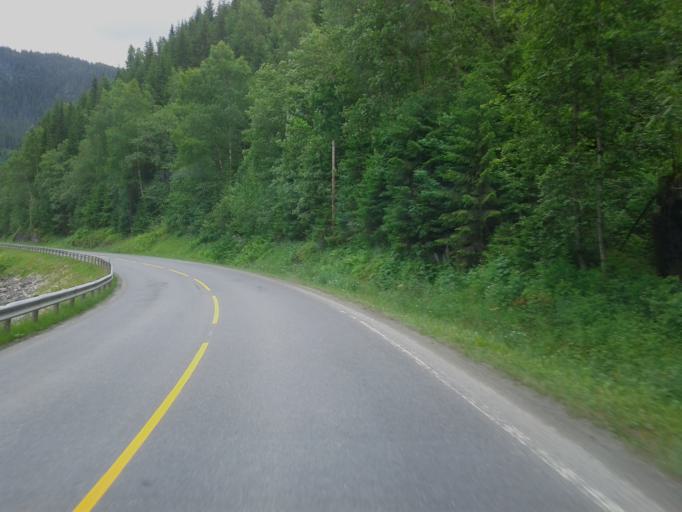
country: NO
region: Sor-Trondelag
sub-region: Midtre Gauldal
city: Storen
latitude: 62.9905
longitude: 10.5208
